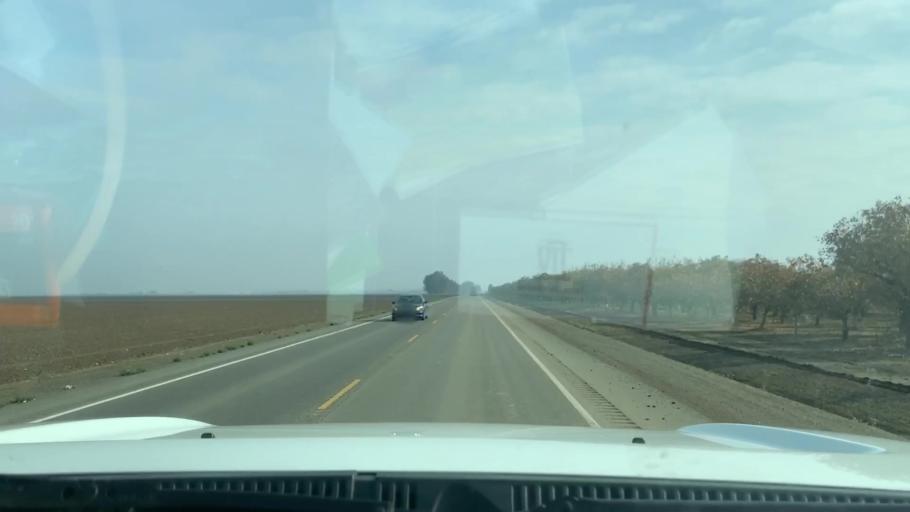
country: US
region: California
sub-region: Kings County
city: Lemoore Station
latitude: 36.2555
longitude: -119.9489
